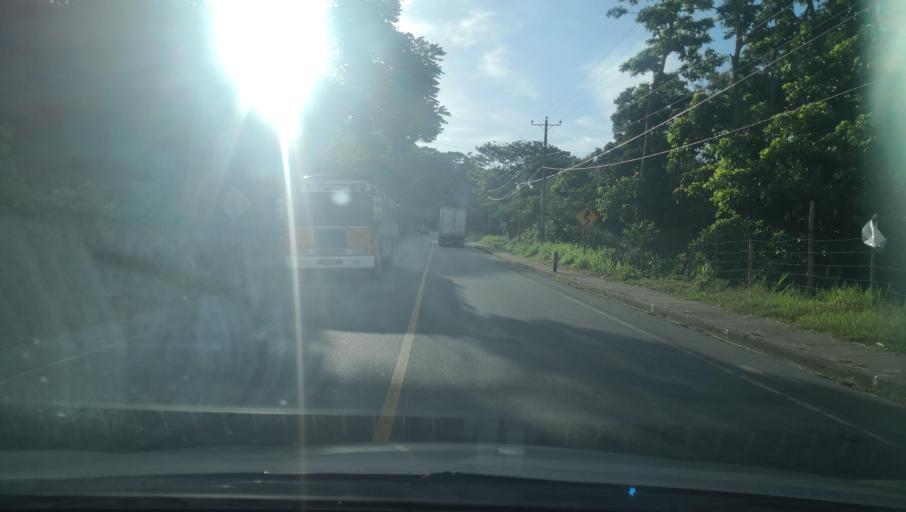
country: HN
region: El Paraiso
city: El Paraiso
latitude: 13.7865
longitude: -86.5617
